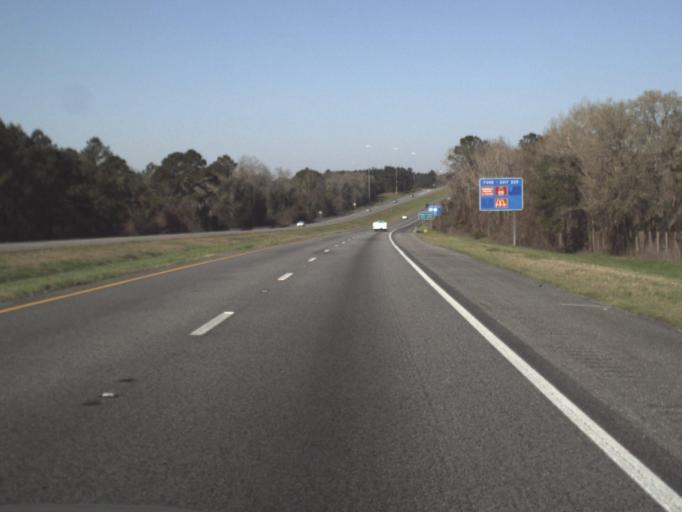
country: US
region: Florida
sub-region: Jefferson County
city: Monticello
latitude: 30.4736
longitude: -83.8766
